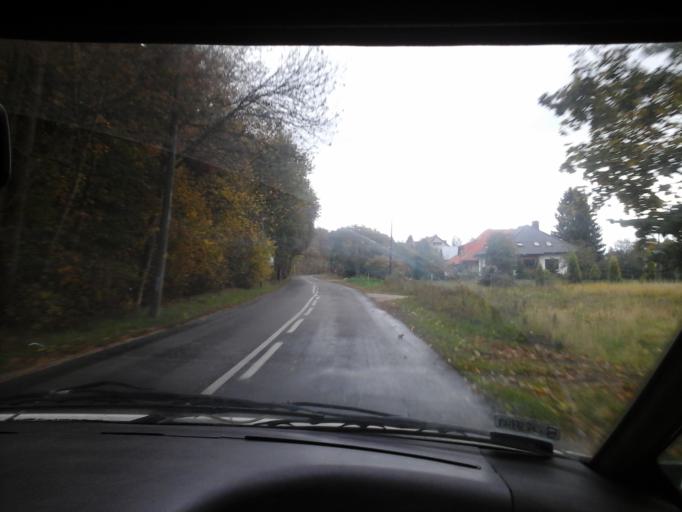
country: PL
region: Pomeranian Voivodeship
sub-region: Powiat gdanski
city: Cedry Wielkie
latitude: 54.3428
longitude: 18.8402
